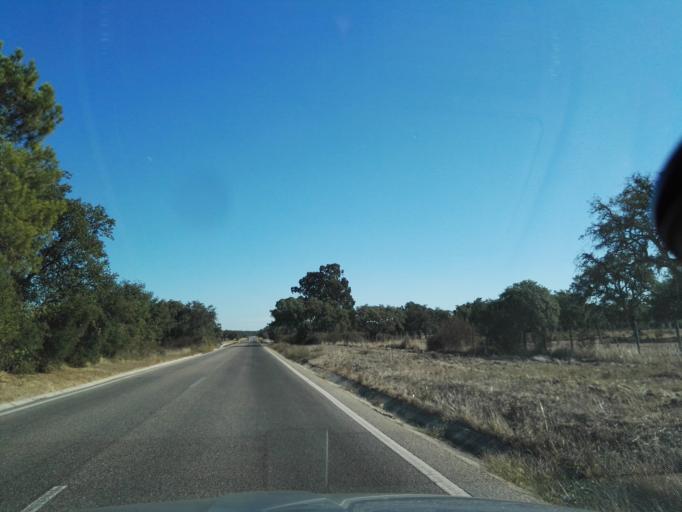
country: PT
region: Santarem
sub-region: Benavente
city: Poceirao
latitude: 38.8997
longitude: -8.7547
